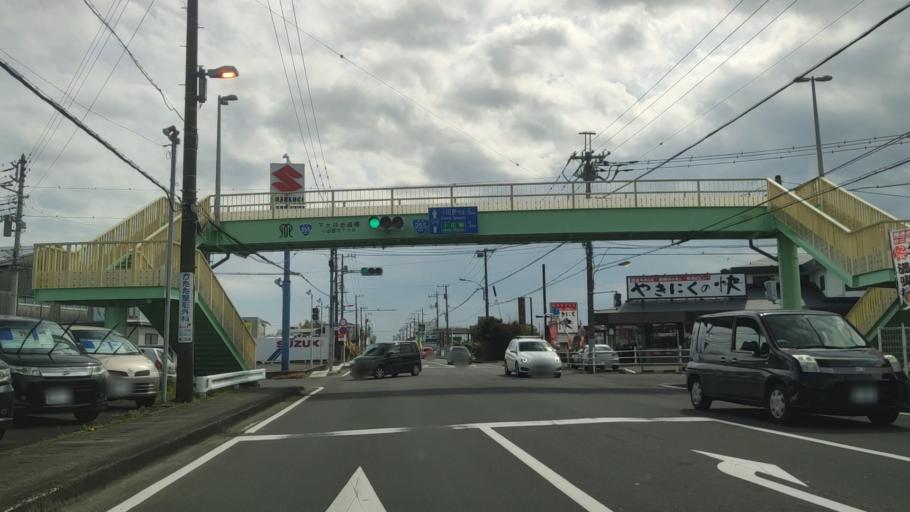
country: JP
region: Kanagawa
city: Odawara
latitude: 35.3144
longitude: 139.1614
